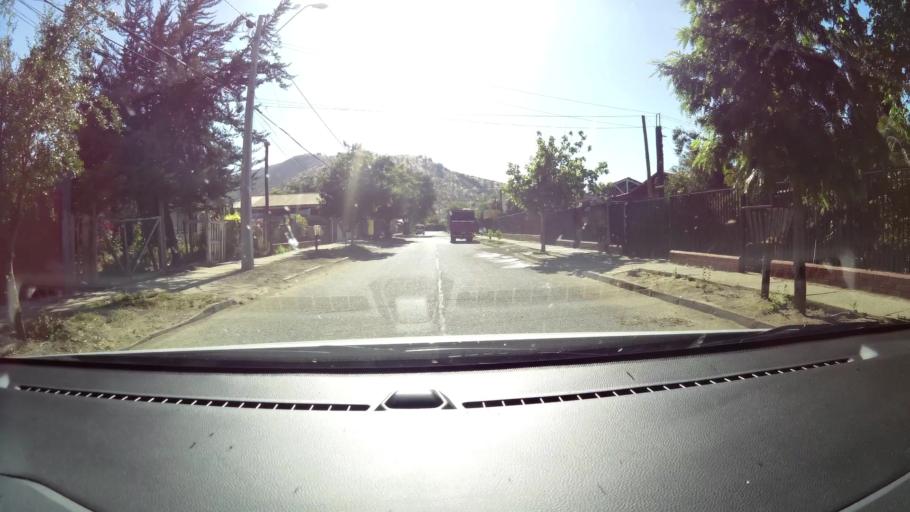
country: CL
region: Santiago Metropolitan
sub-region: Provincia de Chacabuco
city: Lampa
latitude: -33.3971
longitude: -71.1264
